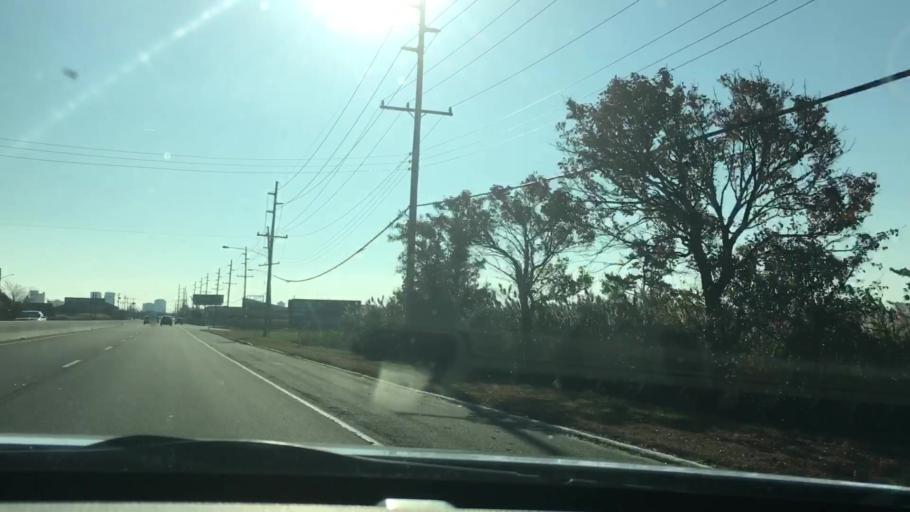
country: US
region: New Jersey
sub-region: Atlantic County
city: Ventnor City
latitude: 39.3741
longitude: -74.4817
